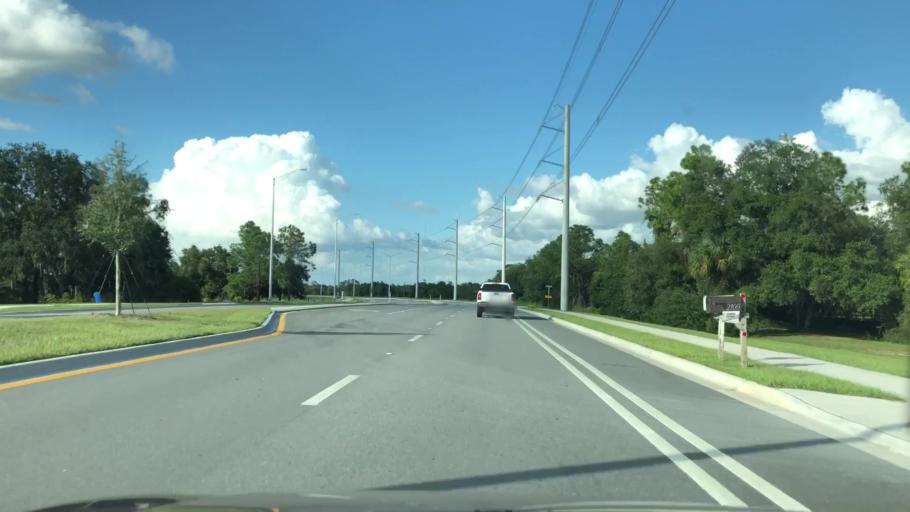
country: US
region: Florida
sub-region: Sarasota County
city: Fruitville
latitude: 27.3468
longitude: -82.3836
